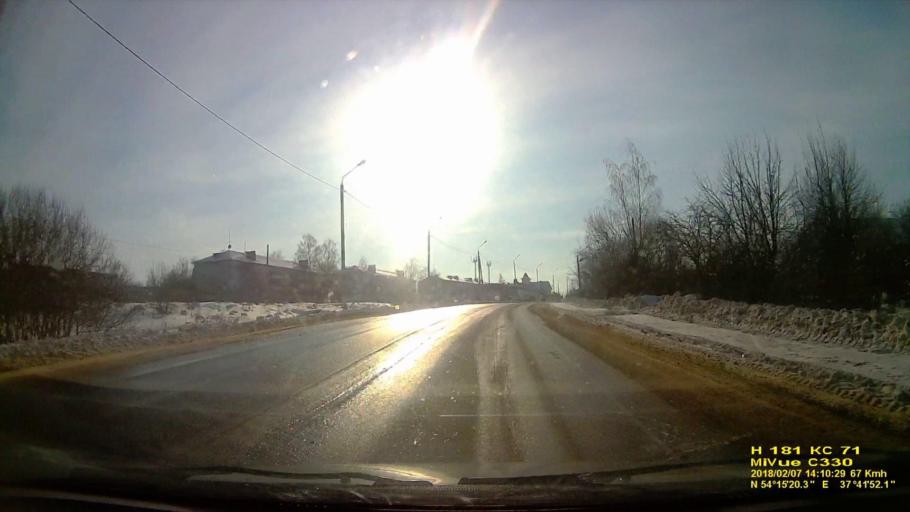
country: RU
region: Tula
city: Gorelki
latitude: 54.2555
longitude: 37.6977
